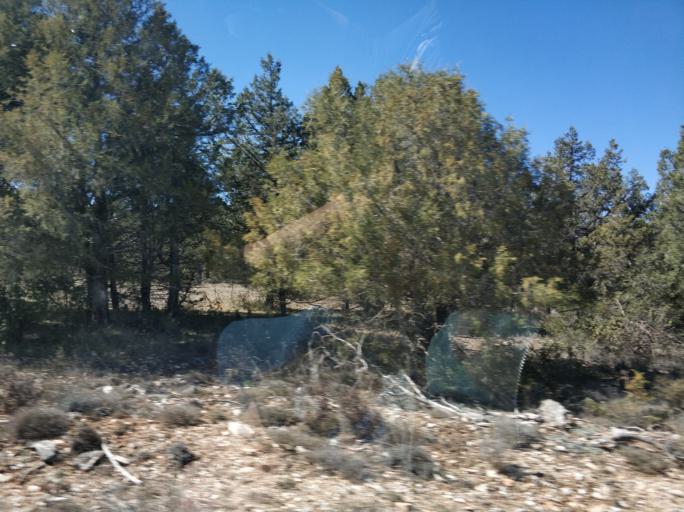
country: ES
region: Castille and Leon
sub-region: Provincia de Soria
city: Ucero
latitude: 41.7366
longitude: -3.0436
